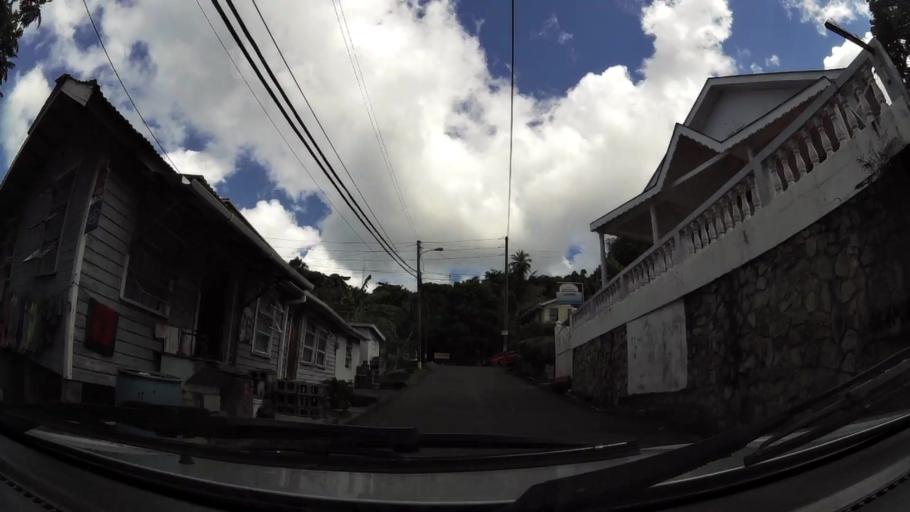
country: GD
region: Saint John
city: Gouyave
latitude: 12.1689
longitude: -61.7274
